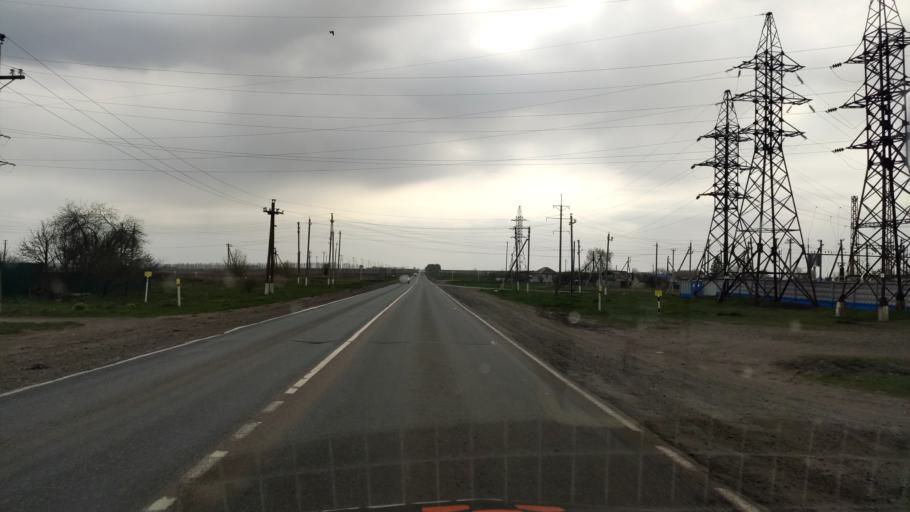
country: RU
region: Kursk
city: Gorshechnoye
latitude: 51.5164
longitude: 38.0120
